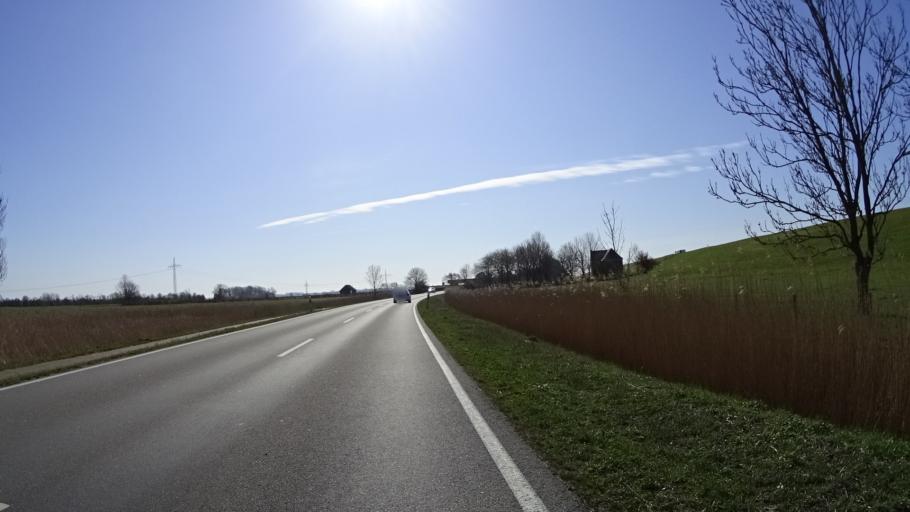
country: DE
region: Lower Saxony
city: Jemgum
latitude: 53.2945
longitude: 7.3979
